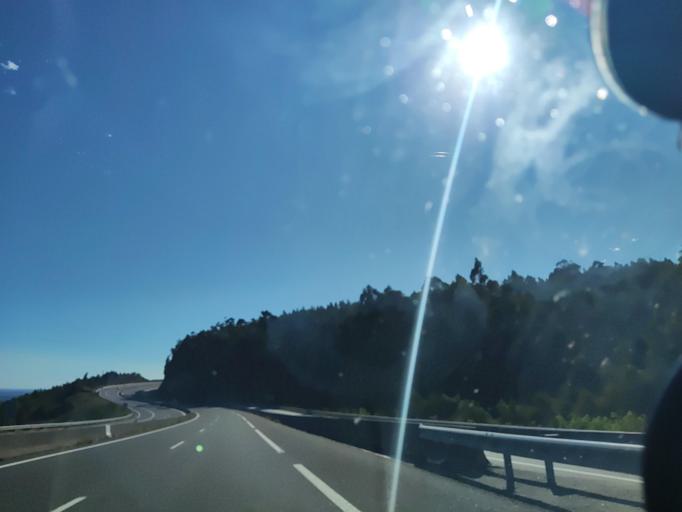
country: ES
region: Galicia
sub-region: Provincia da Coruna
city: Boiro
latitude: 42.6623
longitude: -8.8713
